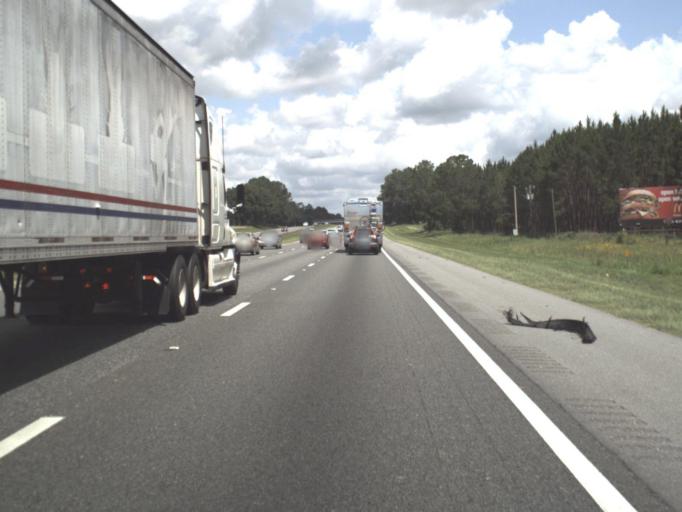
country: US
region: Florida
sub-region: Suwannee County
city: Wellborn
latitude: 30.2861
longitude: -82.7706
